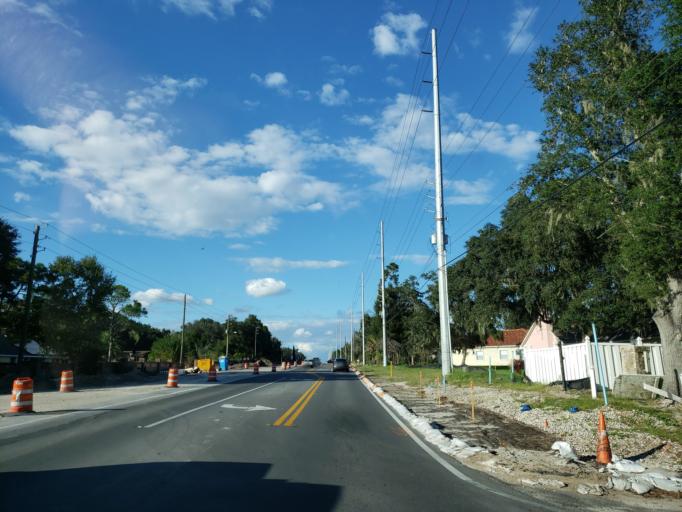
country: US
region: Florida
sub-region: Hillsborough County
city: Bloomingdale
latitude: 27.8650
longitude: -82.2692
